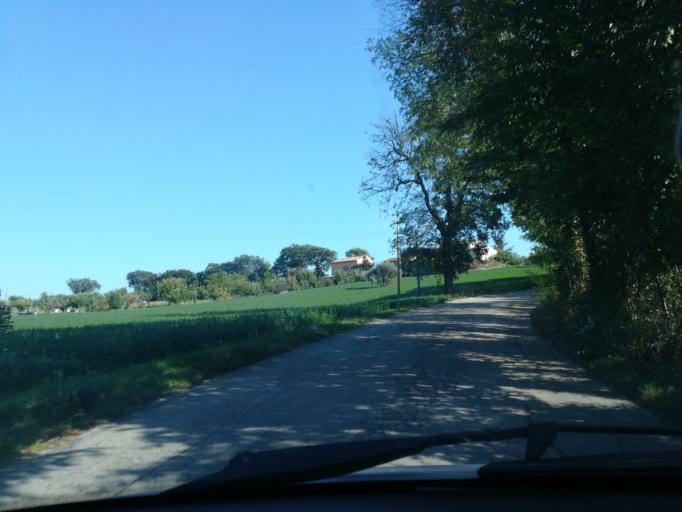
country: IT
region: The Marches
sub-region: Provincia di Macerata
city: Piediripa
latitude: 43.2976
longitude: 13.4819
